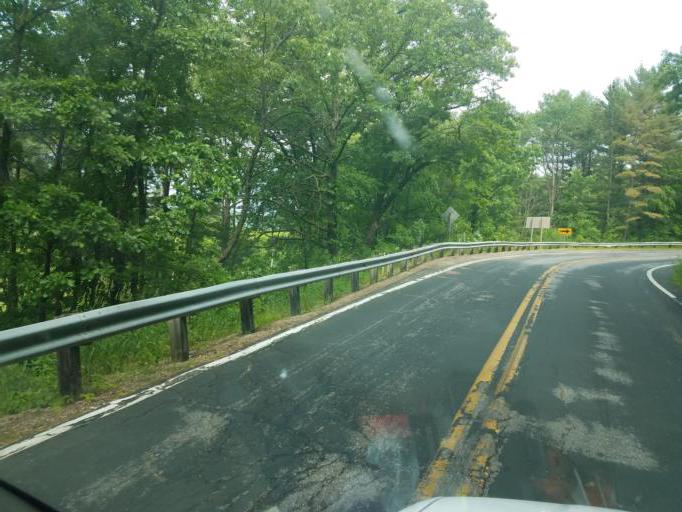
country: US
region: Wisconsin
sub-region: Monroe County
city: Cashton
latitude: 43.7116
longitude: -90.5816
